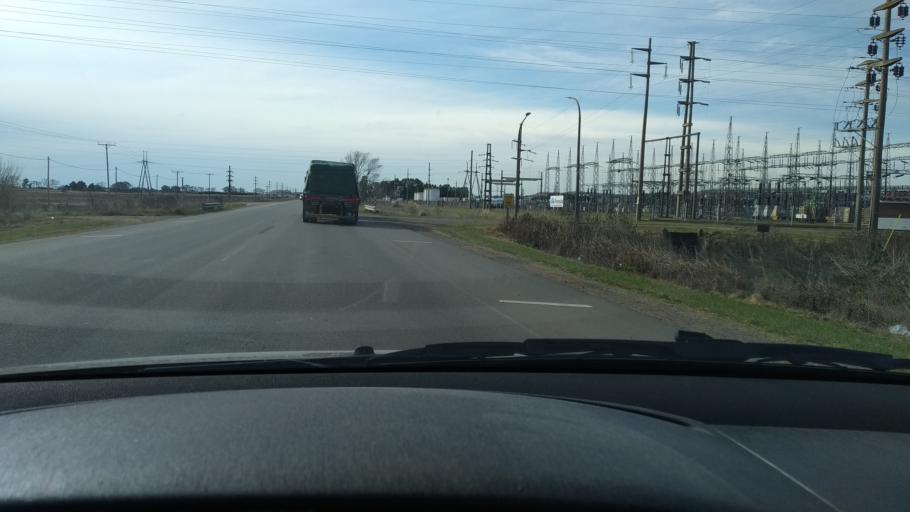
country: AR
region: Buenos Aires
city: Olavarria
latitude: -36.9449
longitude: -60.2403
